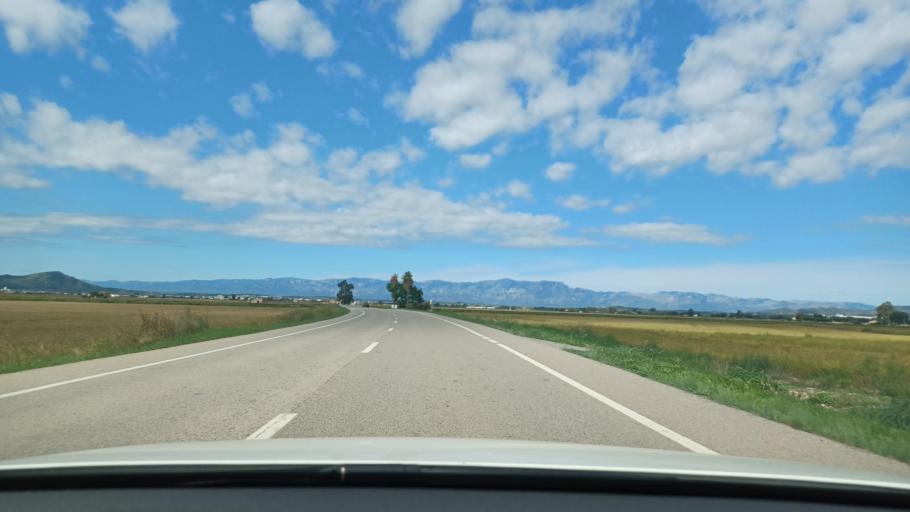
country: ES
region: Catalonia
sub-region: Provincia de Tarragona
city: Deltebre
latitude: 40.7027
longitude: 0.6664
